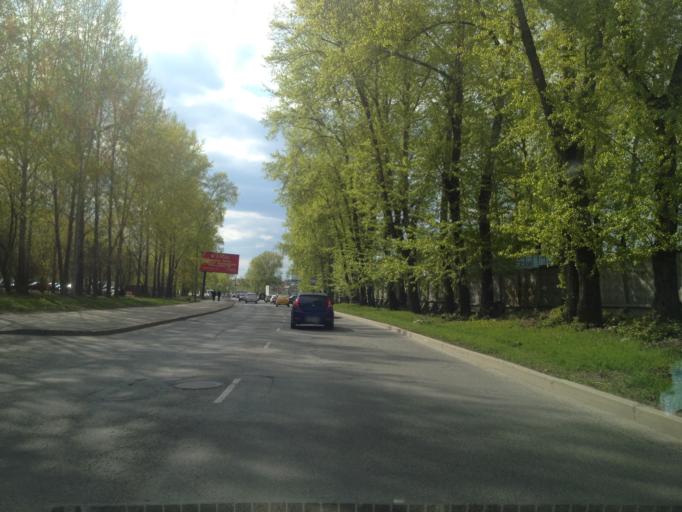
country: RU
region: Sverdlovsk
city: Yekaterinburg
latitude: 56.8573
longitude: 60.5694
